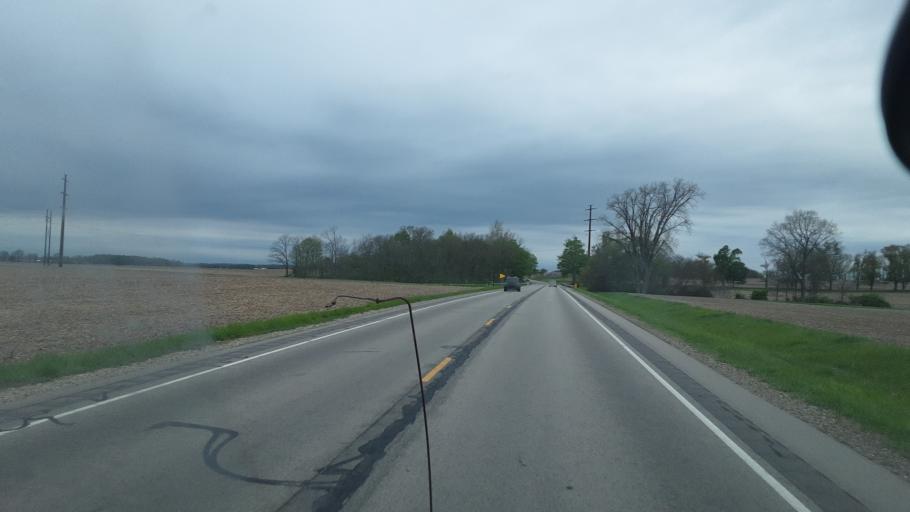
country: US
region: Indiana
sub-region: Kosciusko County
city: Syracuse
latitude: 41.4793
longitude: -85.7050
